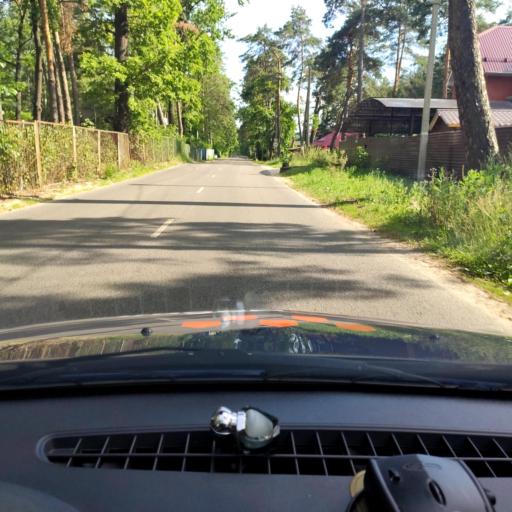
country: RU
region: Voronezj
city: Somovo
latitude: 51.7542
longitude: 39.3660
